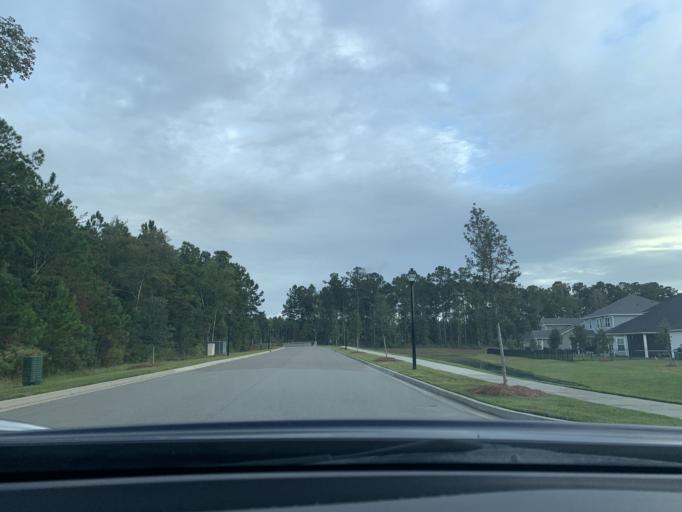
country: US
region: Georgia
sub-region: Chatham County
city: Pooler
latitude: 32.0717
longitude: -81.2584
